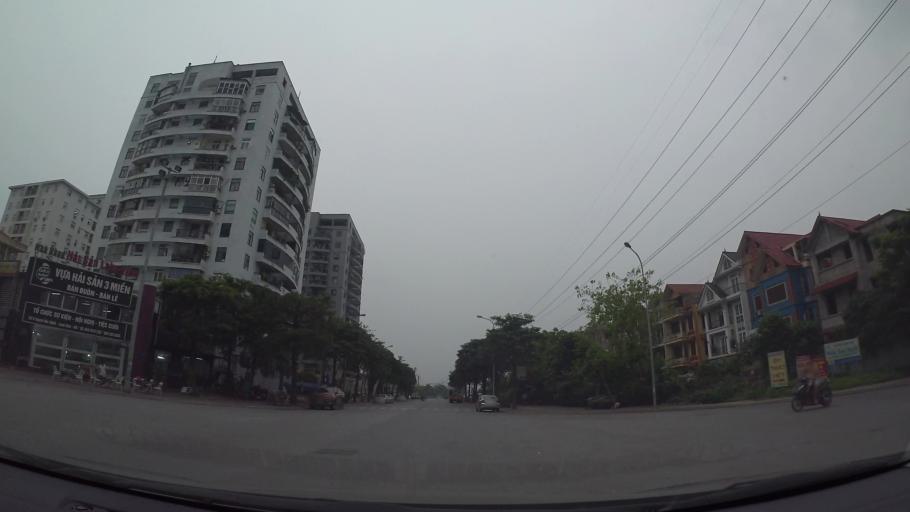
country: VN
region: Ha Noi
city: Trau Quy
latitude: 21.0364
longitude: 105.9065
